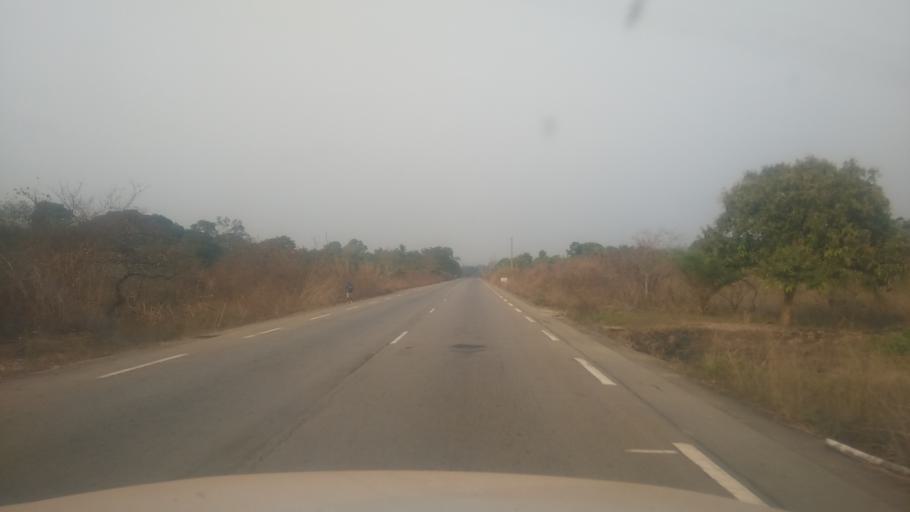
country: CM
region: Centre
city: Bafia
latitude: 4.8261
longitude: 11.0501
